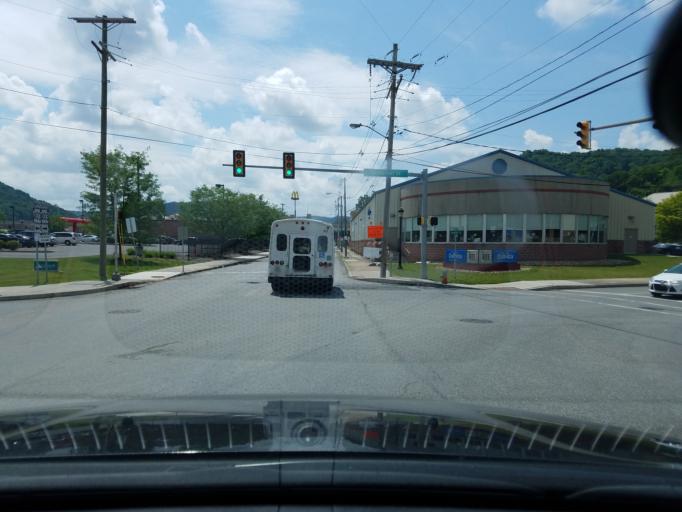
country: US
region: Pennsylvania
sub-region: Cambria County
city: Johnstown
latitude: 40.3222
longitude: -78.9209
